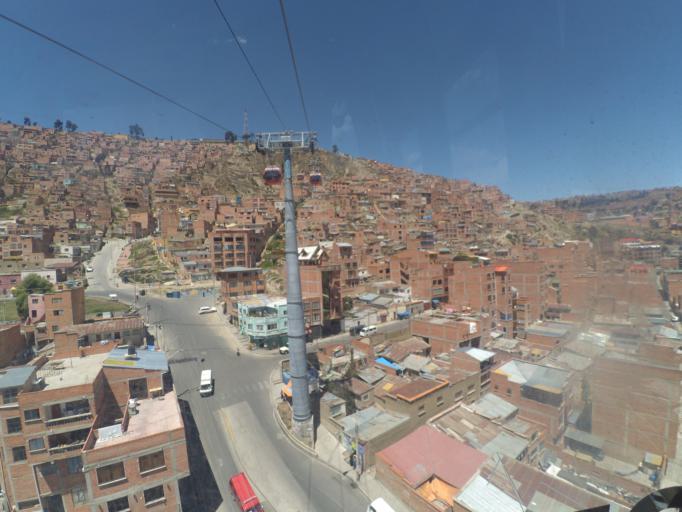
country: BO
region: La Paz
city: La Paz
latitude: -16.4977
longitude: -68.1589
